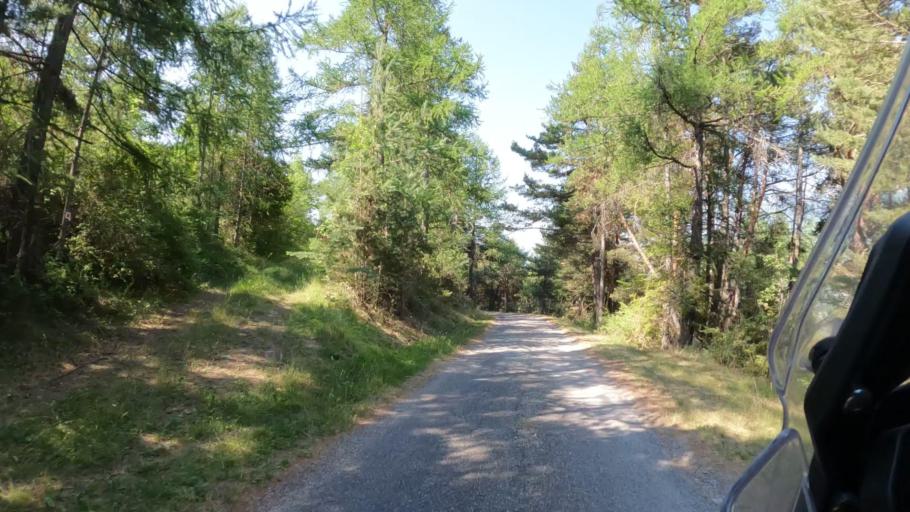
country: FR
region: Provence-Alpes-Cote d'Azur
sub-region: Departement des Hautes-Alpes
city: Embrun
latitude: 44.5945
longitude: 6.5456
